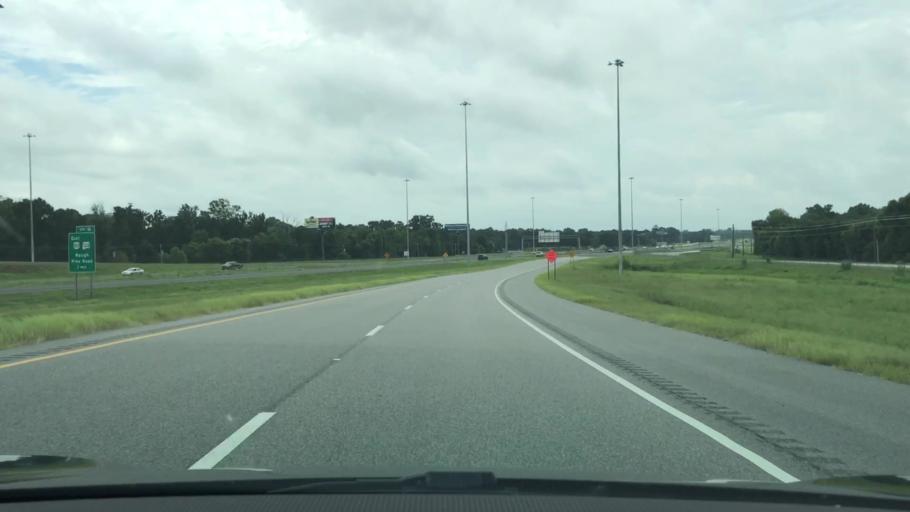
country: US
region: Alabama
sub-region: Montgomery County
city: Pike Road
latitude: 32.3674
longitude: -86.0747
